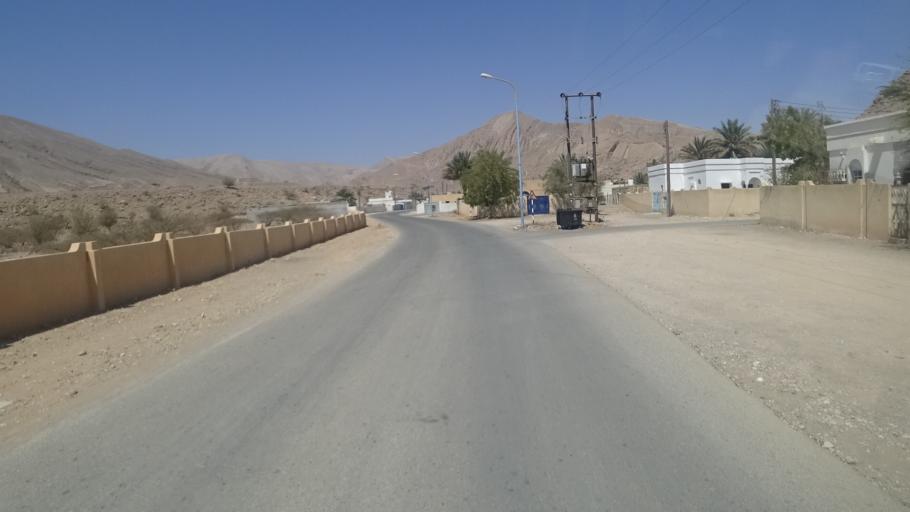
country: OM
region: Ash Sharqiyah
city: Badiyah
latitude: 22.5919
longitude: 59.0882
